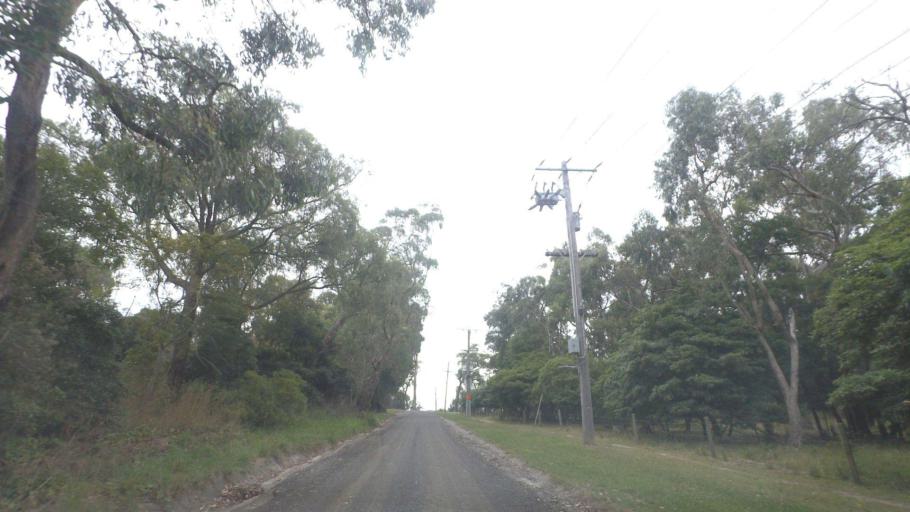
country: AU
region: Victoria
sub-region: Yarra Ranges
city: Mount Evelyn
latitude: -37.7632
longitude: 145.3752
